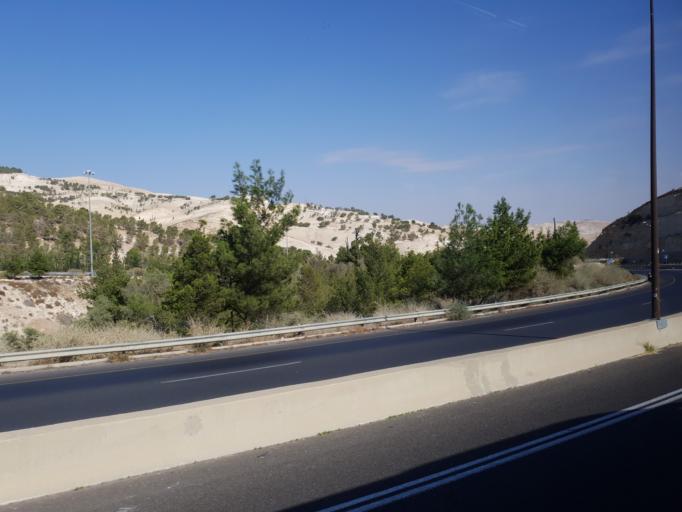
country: PS
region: West Bank
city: Al `Ayzariyah
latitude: 31.7844
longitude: 35.2925
